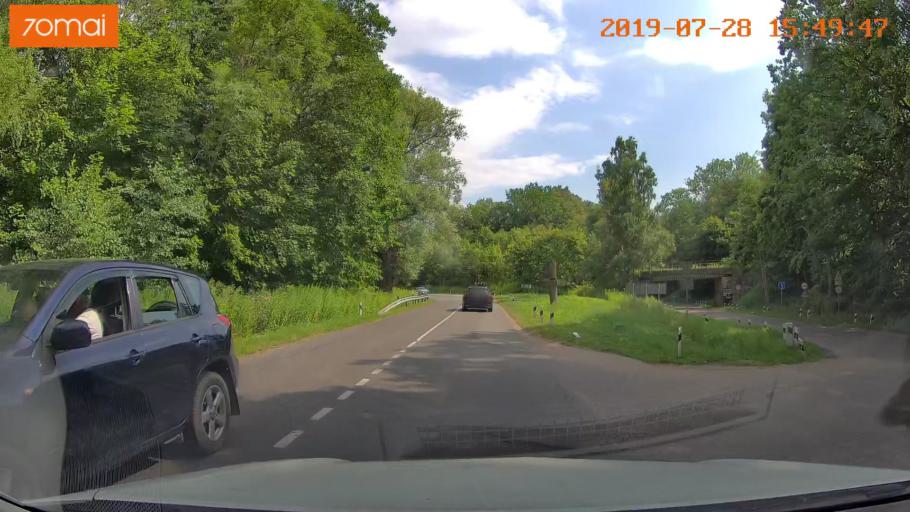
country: RU
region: Kaliningrad
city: Otradnoye
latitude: 54.9406
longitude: 20.0826
